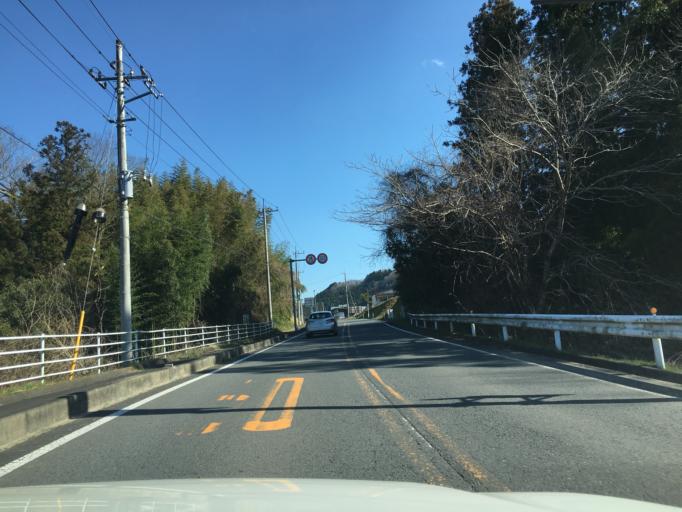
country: JP
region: Tochigi
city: Motegi
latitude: 36.5645
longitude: 140.2463
